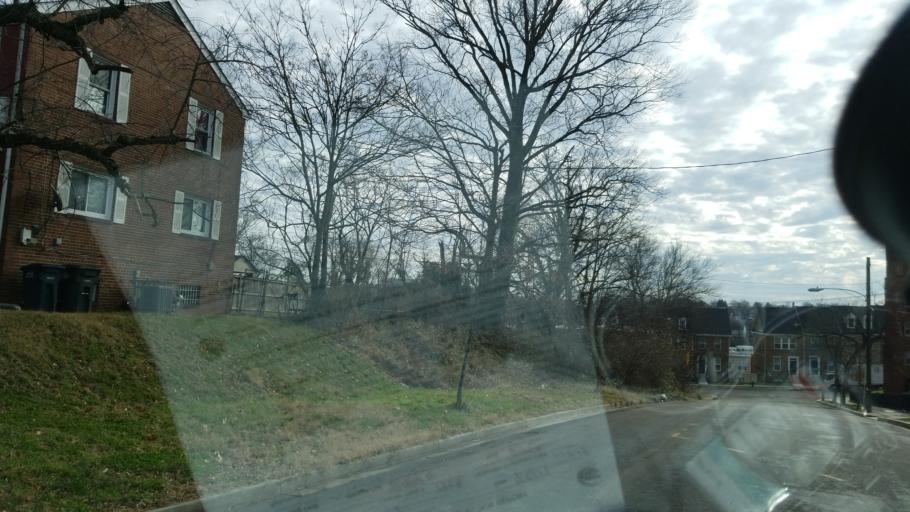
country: US
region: Maryland
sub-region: Prince George's County
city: Glassmanor
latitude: 38.8414
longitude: -76.9901
